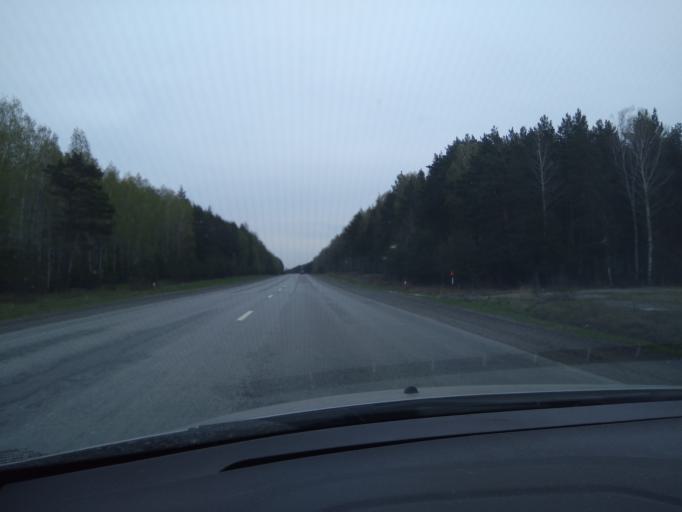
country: RU
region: Sverdlovsk
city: Baraba
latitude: 56.7828
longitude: 61.7715
